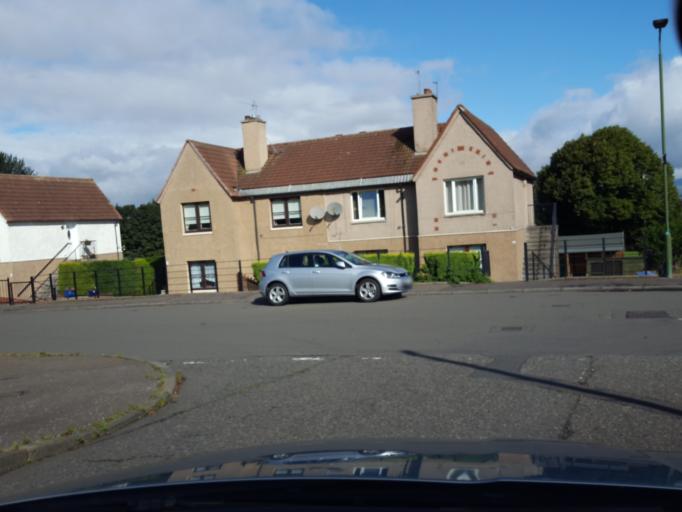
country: GB
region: Scotland
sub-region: Falkirk
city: Bo'ness
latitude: 56.0125
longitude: -3.6199
